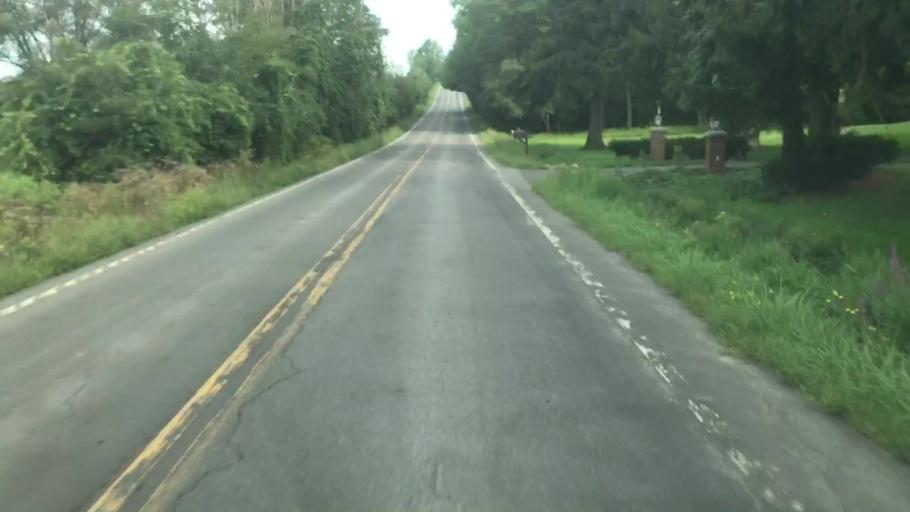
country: US
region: New York
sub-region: Onondaga County
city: Skaneateles
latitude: 42.8873
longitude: -76.4490
